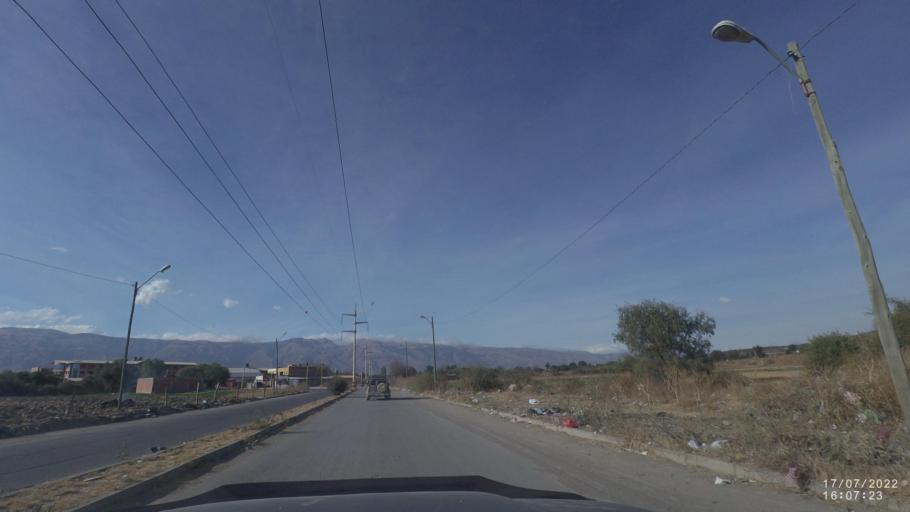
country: BO
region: Cochabamba
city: Sipe Sipe
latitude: -17.4145
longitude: -66.2728
